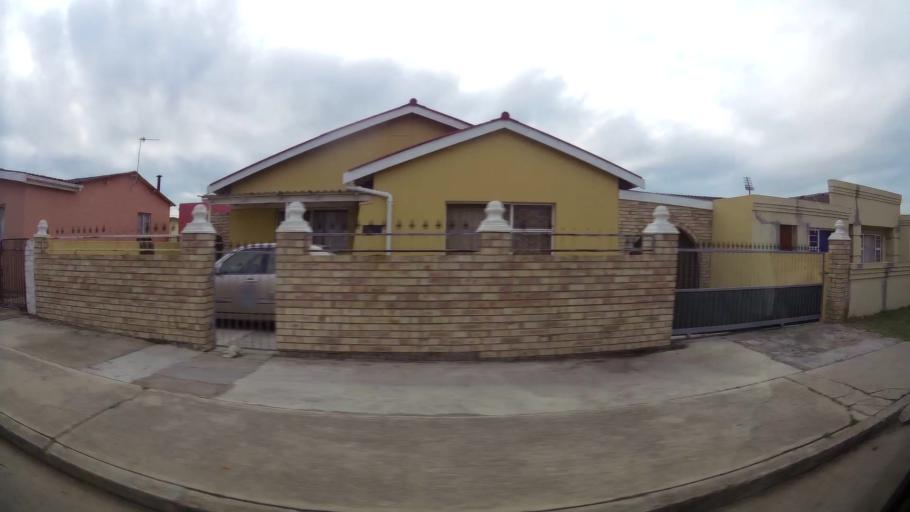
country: ZA
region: Eastern Cape
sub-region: Nelson Mandela Bay Metropolitan Municipality
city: Port Elizabeth
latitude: -33.9131
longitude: 25.5569
